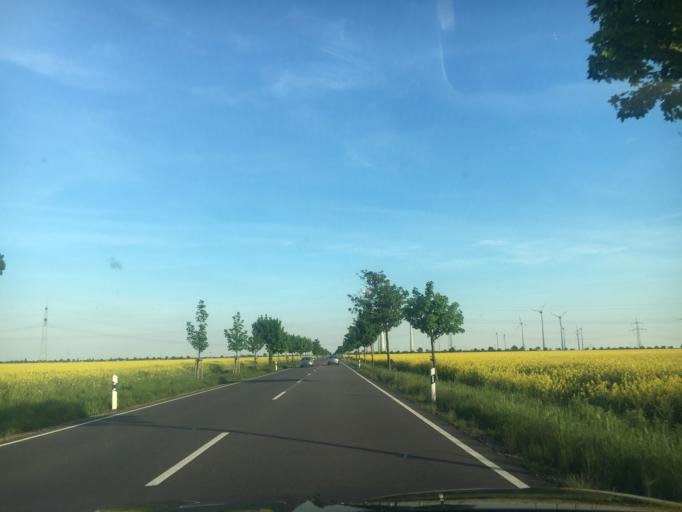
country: DE
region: Saxony-Anhalt
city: Raguhn
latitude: 51.7280
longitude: 12.2337
